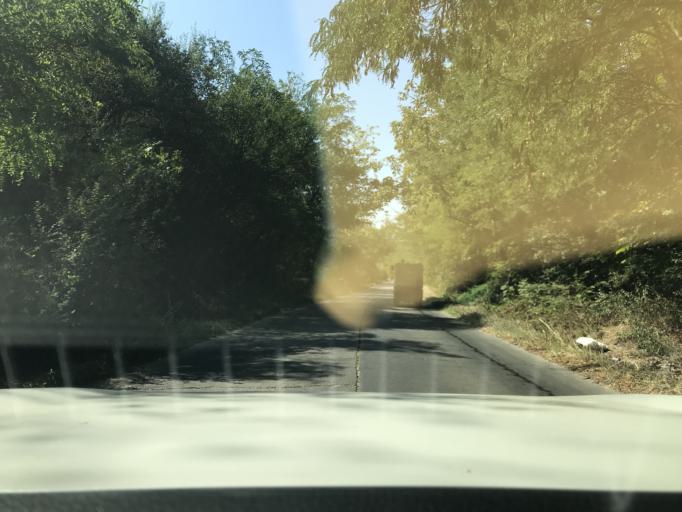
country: RO
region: Olt
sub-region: Municipiul Slatina
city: Slatina
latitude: 44.4128
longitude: 24.3607
